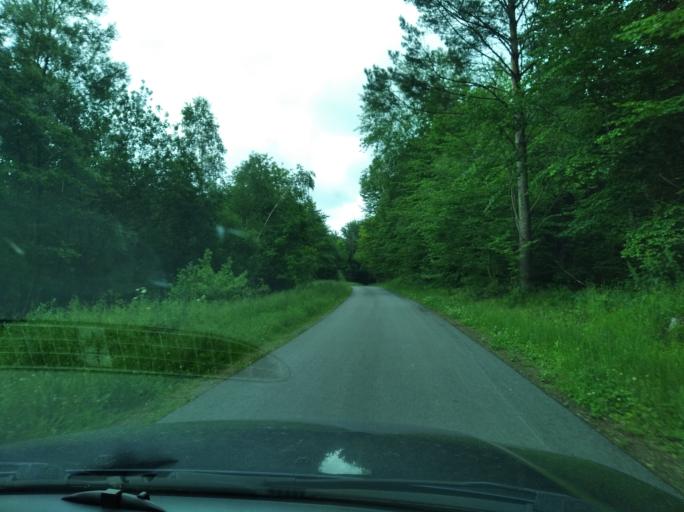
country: PL
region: Subcarpathian Voivodeship
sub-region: Powiat przemyski
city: Przedmiescie Dubieckie
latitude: 49.8746
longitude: 22.4038
